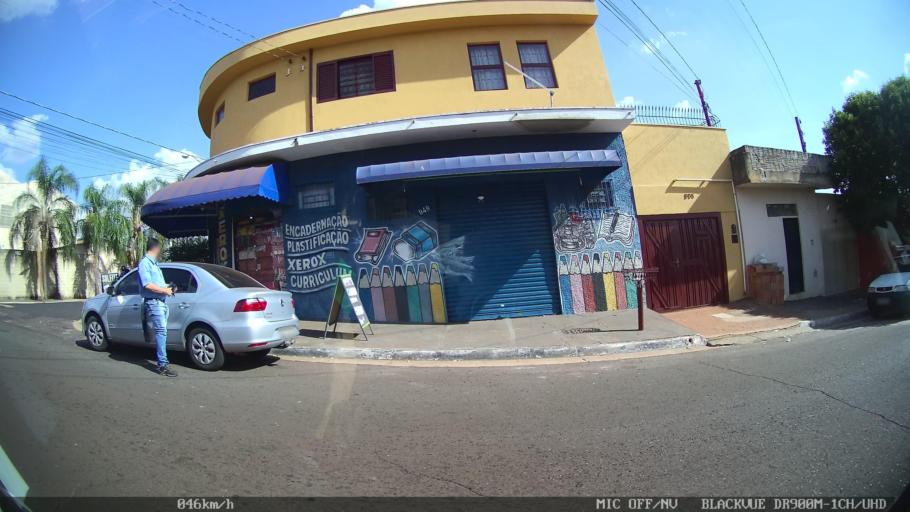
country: BR
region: Sao Paulo
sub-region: Ribeirao Preto
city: Ribeirao Preto
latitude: -21.1970
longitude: -47.8494
